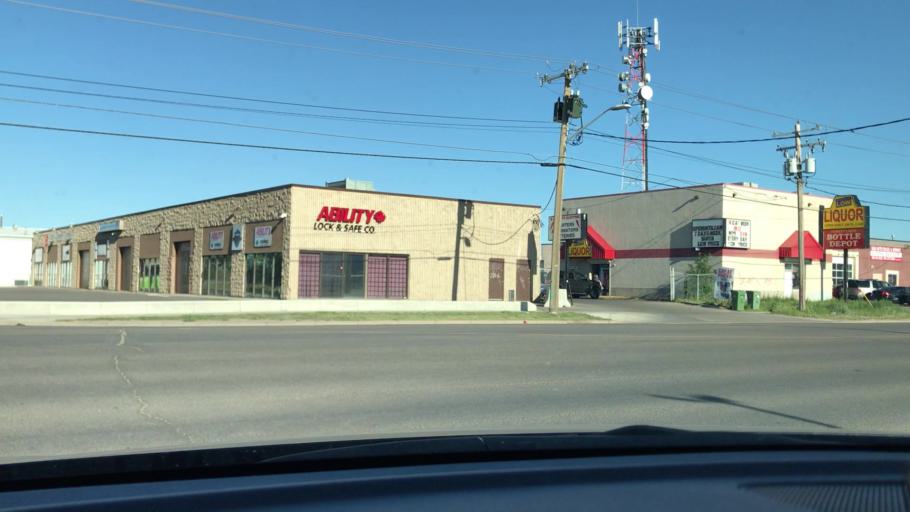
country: CA
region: Alberta
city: Calgary
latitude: 51.0344
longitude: -113.9586
